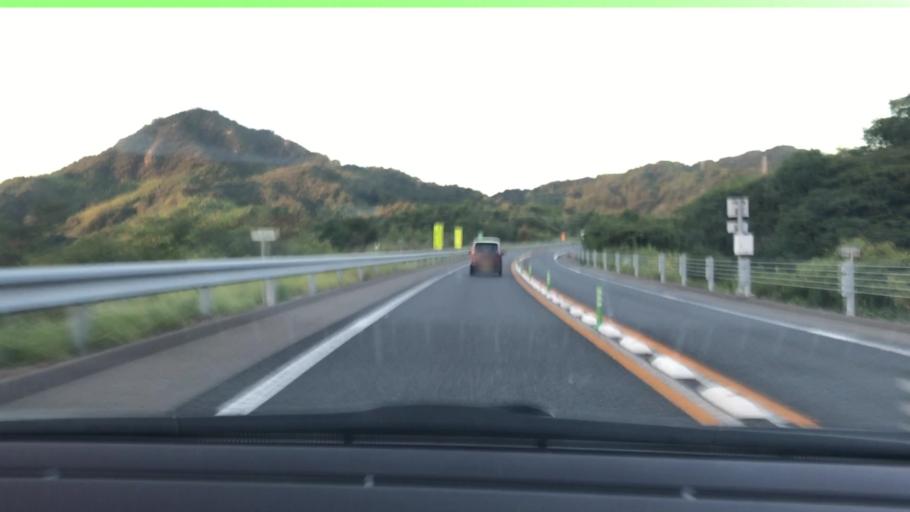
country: JP
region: Hiroshima
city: Innoshima
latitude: 34.3333
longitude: 133.1562
